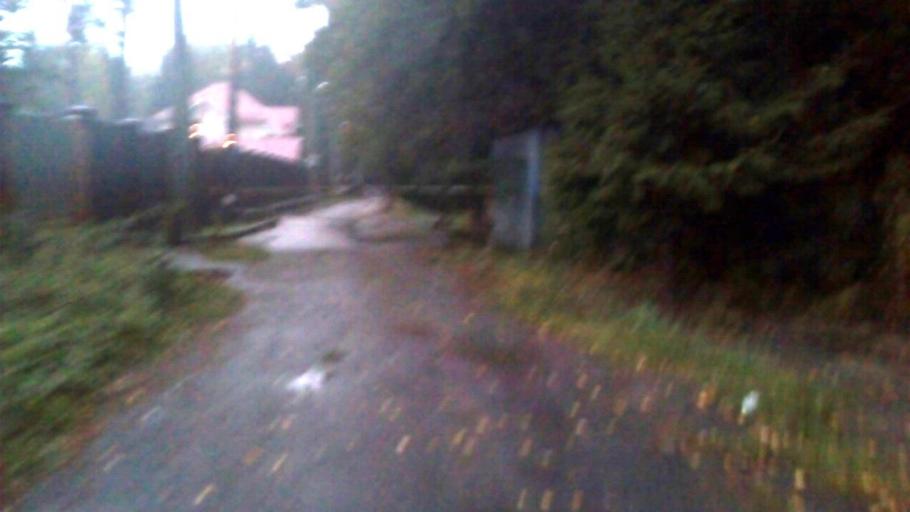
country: RU
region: Moskovskaya
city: Lesnoy Gorodok
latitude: 55.6718
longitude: 37.1906
